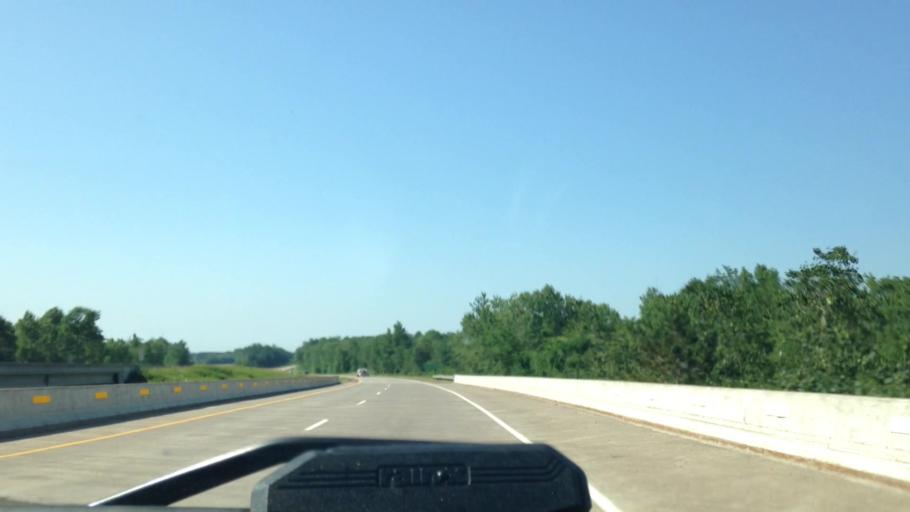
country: US
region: Wisconsin
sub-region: Douglas County
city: Lake Nebagamon
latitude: 46.3981
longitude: -91.8184
